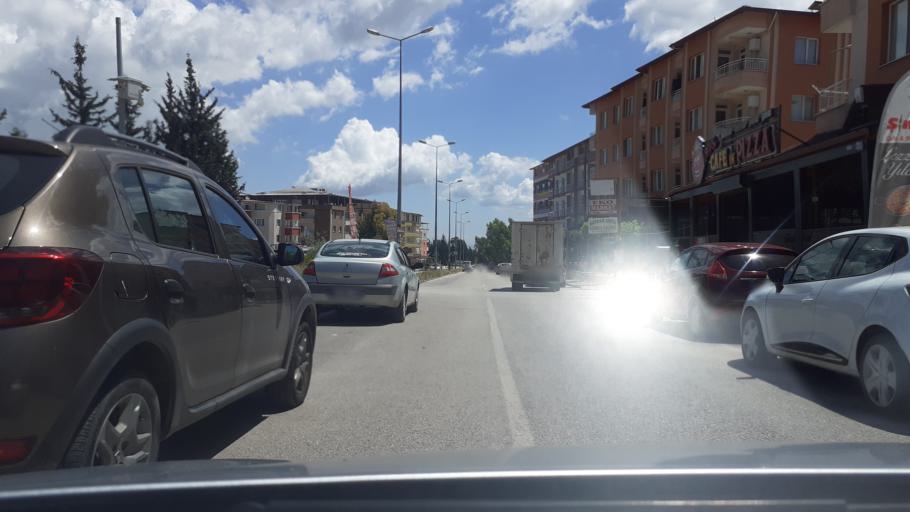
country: TR
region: Hatay
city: Anayazi
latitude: 36.3348
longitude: 36.2020
